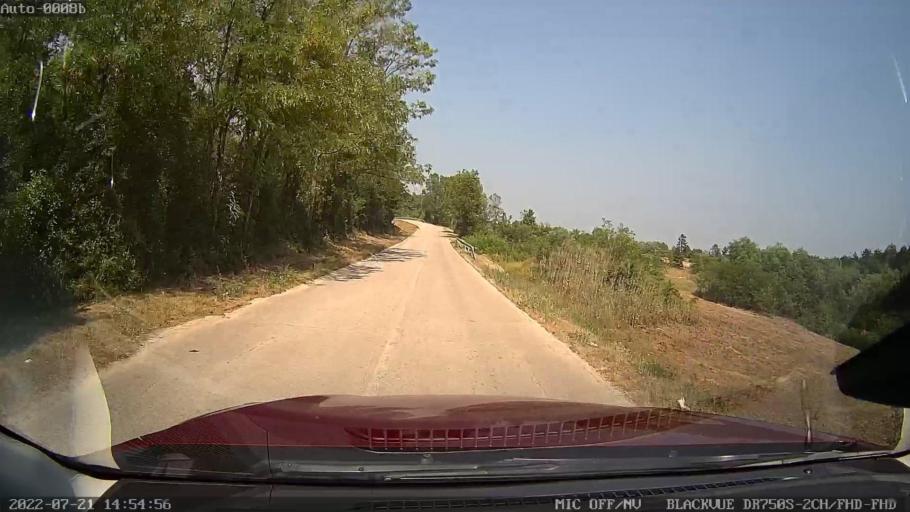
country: HR
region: Istarska
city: Pazin
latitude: 45.1920
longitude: 13.9403
